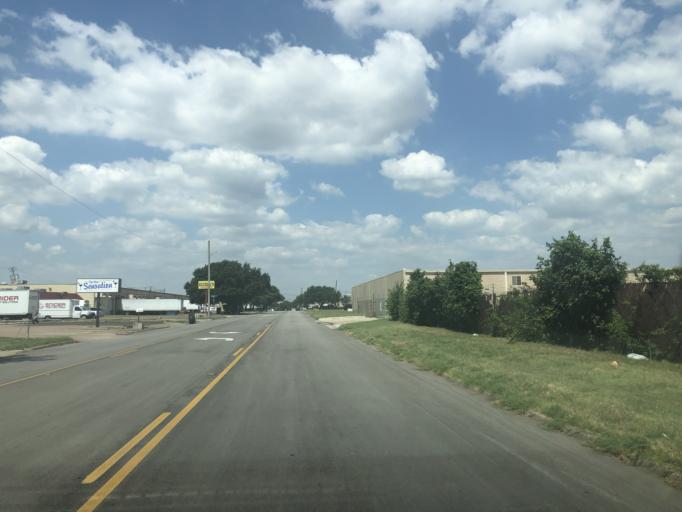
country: US
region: Texas
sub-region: Dallas County
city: Grand Prairie
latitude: 32.7447
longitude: -97.0411
